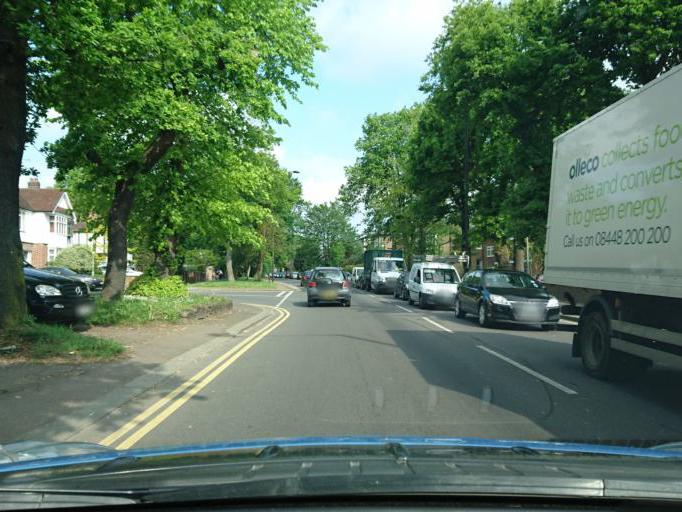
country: GB
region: England
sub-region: Greater London
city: Wood Green
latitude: 51.6350
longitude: -0.1349
